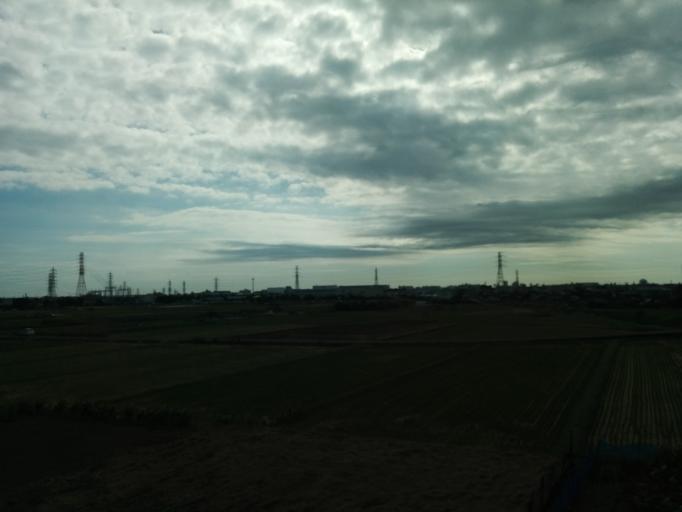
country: JP
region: Kanagawa
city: Isehara
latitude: 35.3661
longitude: 139.3349
